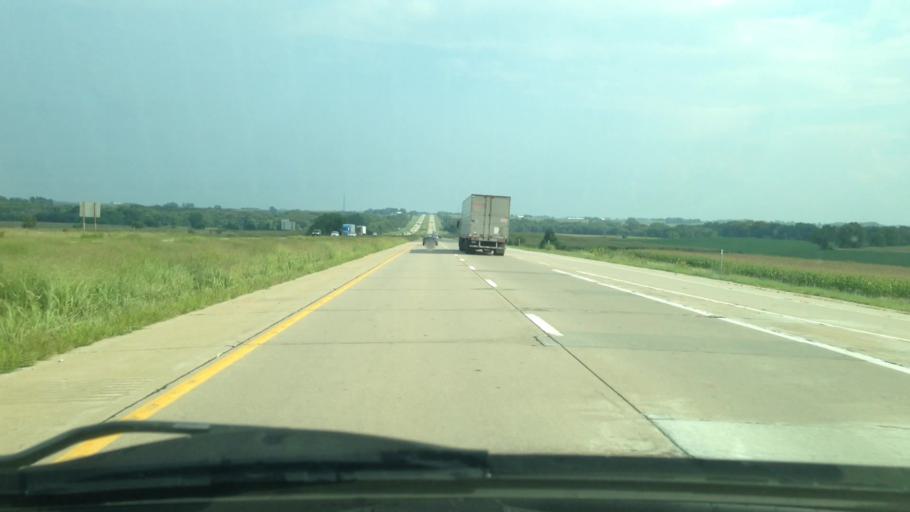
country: US
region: Iowa
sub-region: Benton County
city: Urbana
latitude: 42.3098
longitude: -91.9751
